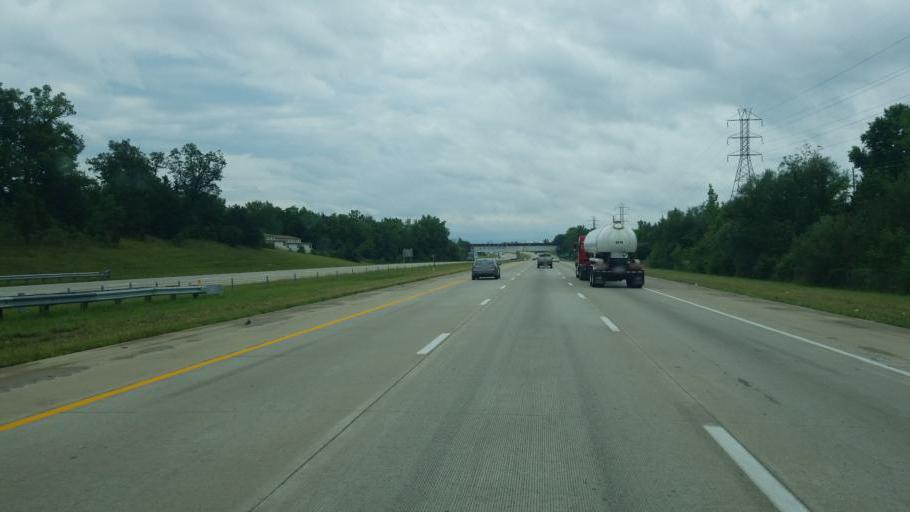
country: US
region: Ohio
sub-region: Franklin County
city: Lincoln Village
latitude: 39.9400
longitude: -83.1224
